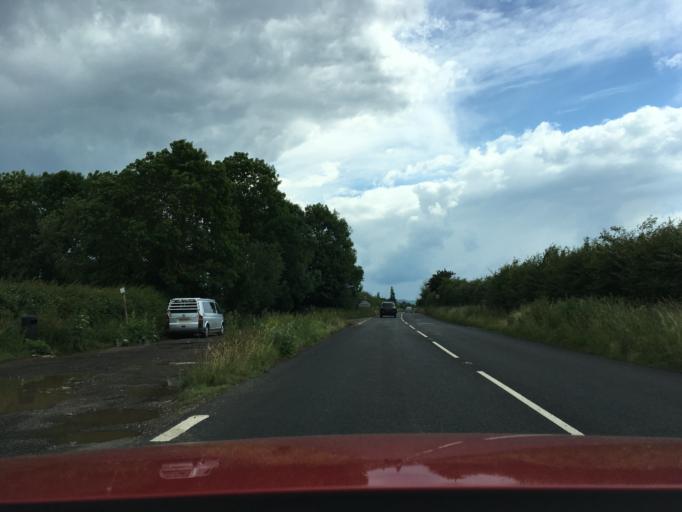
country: GB
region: England
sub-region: Gloucestershire
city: Stonehouse
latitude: 51.7859
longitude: -2.2895
